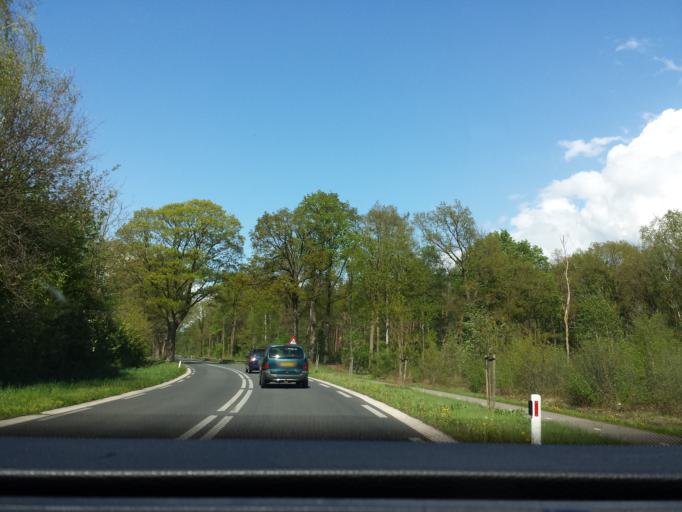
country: NL
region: Gelderland
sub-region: Gemeente Lochem
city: Barchem
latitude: 52.0568
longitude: 6.4258
